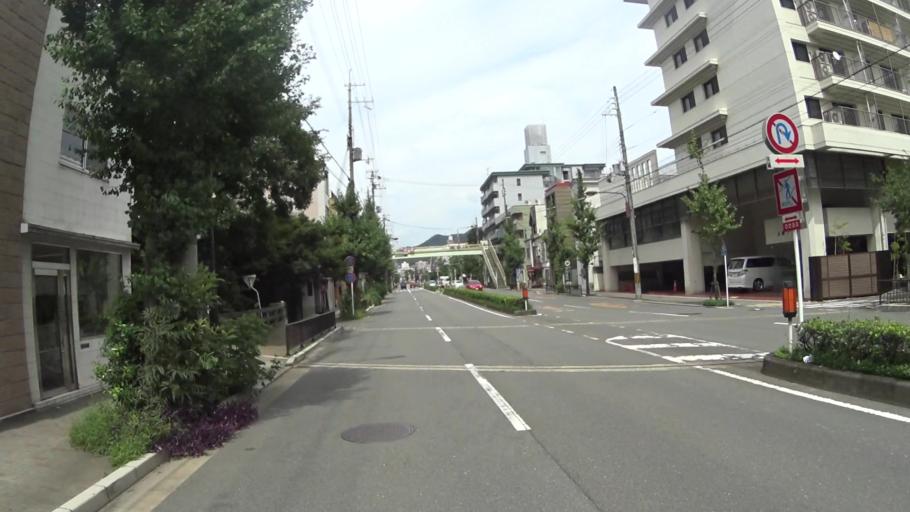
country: JP
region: Kyoto
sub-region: Kyoto-shi
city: Kamigyo-ku
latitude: 35.0185
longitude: 135.7912
